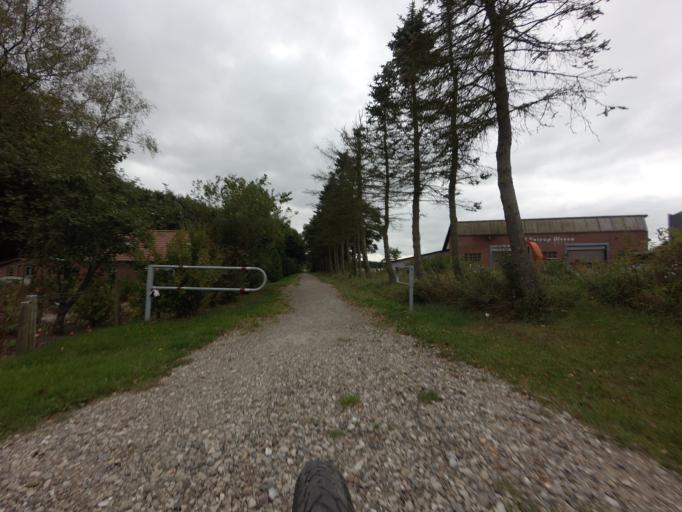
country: DK
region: Central Jutland
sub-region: Ikast-Brande Kommune
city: Brande
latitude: 55.9326
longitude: 9.1434
